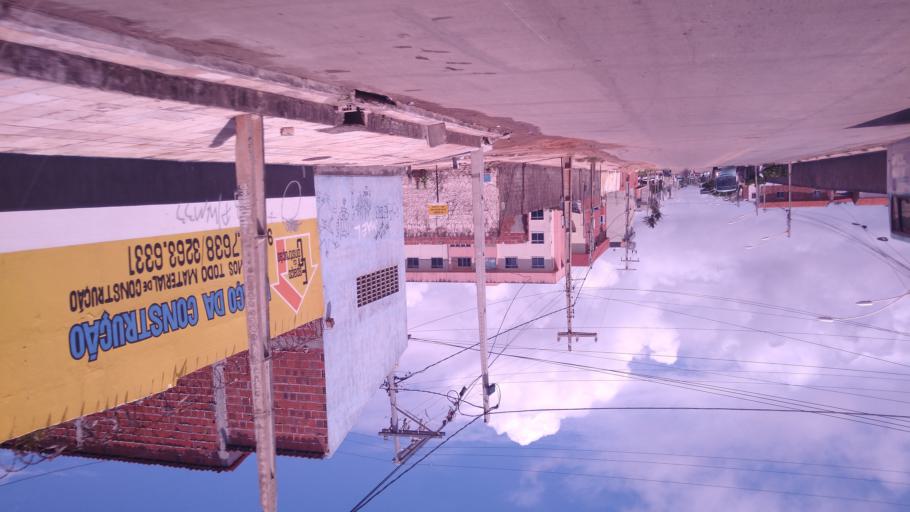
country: BR
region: Ceara
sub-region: Fortaleza
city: Fortaleza
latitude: -3.7205
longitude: -38.4647
